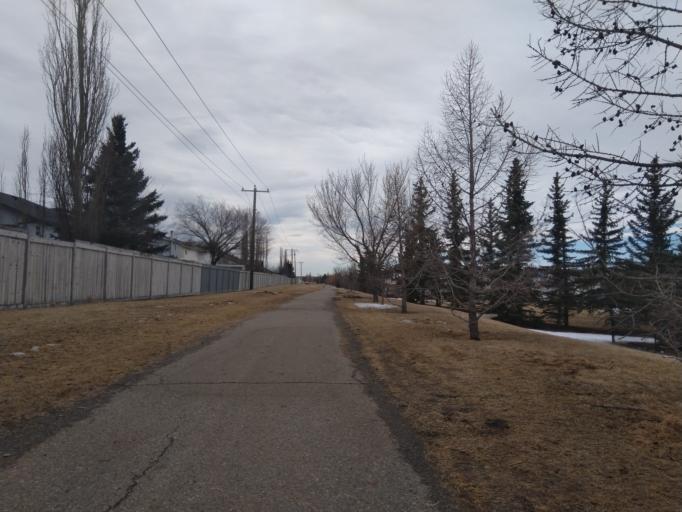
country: CA
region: Alberta
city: Calgary
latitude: 51.1615
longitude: -114.0480
